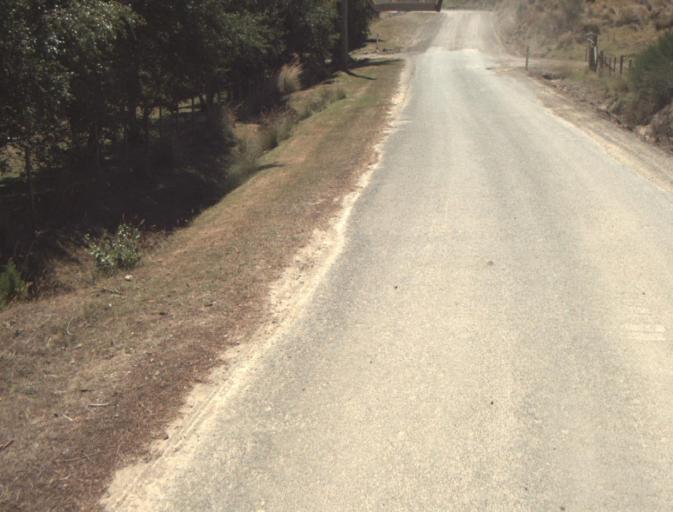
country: AU
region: Tasmania
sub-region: Dorset
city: Scottsdale
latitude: -41.3587
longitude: 147.4606
